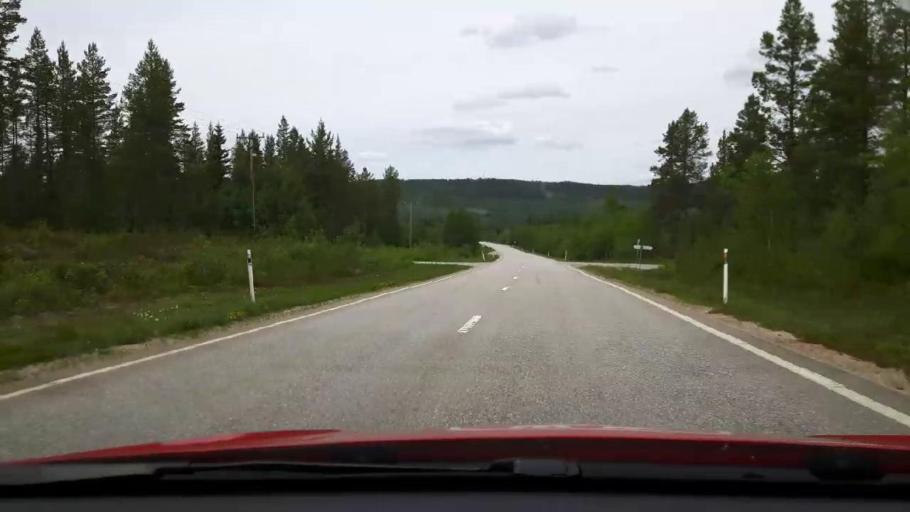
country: SE
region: Jaemtland
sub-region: Harjedalens Kommun
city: Sveg
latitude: 62.0881
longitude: 14.2489
